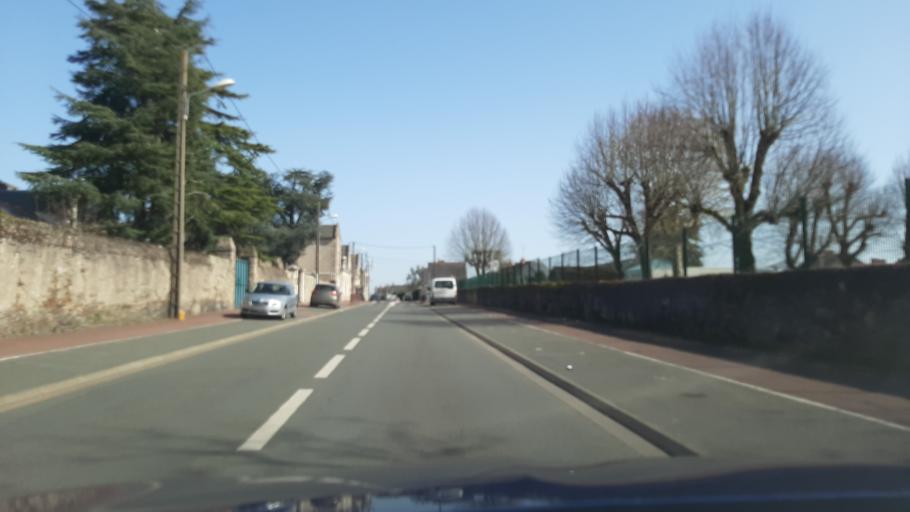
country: FR
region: Pays de la Loire
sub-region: Departement de Maine-et-Loire
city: Les Ponts-de-Ce
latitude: 47.4535
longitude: -0.5199
